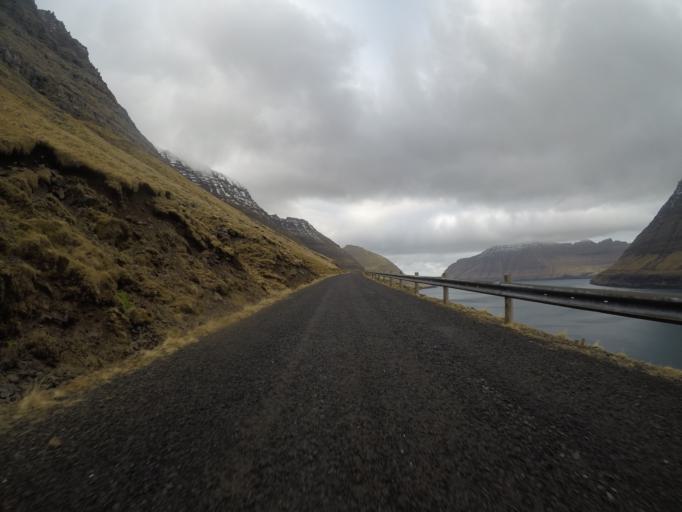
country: FO
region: Nordoyar
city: Klaksvik
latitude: 62.3270
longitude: -6.5676
